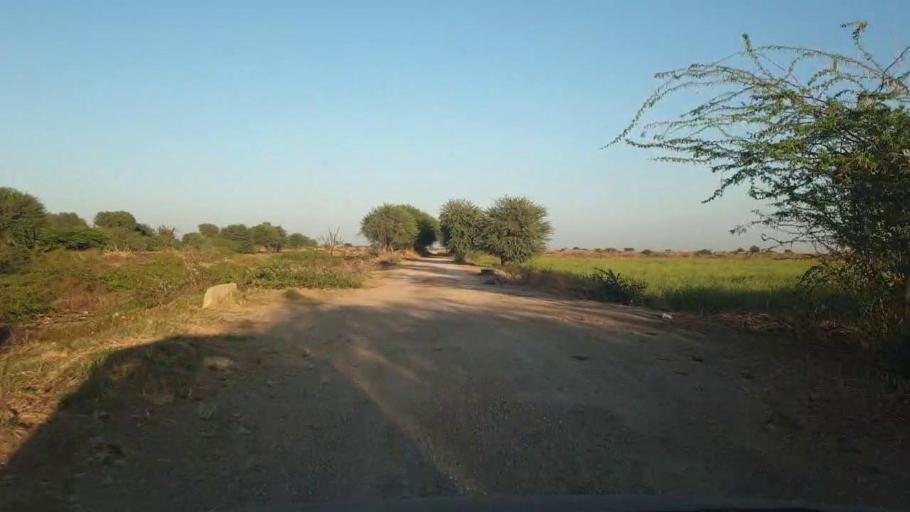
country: PK
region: Sindh
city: Dhoro Naro
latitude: 25.3596
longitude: 69.5750
